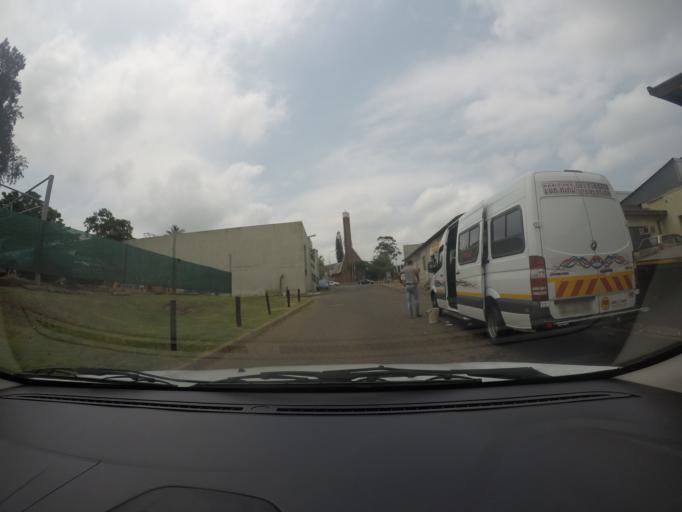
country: ZA
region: KwaZulu-Natal
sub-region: uThungulu District Municipality
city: Empangeni
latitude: -28.7473
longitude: 31.8912
